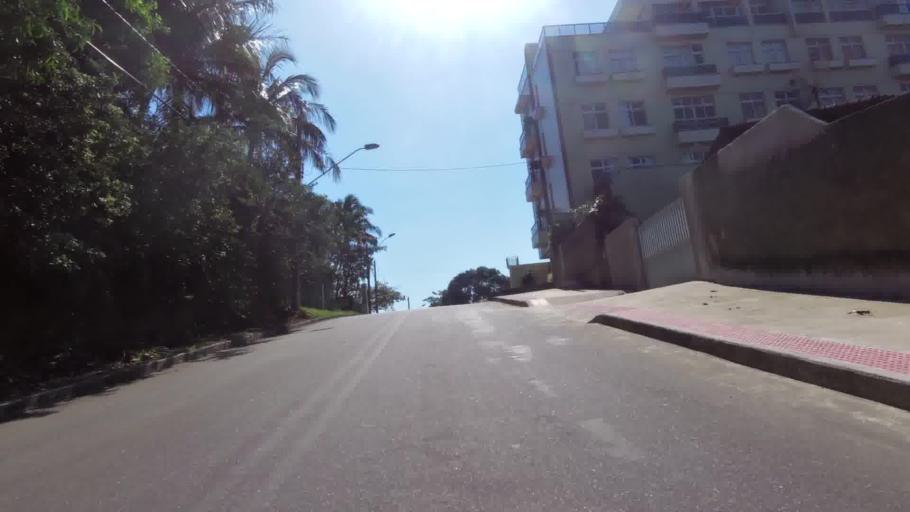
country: BR
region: Espirito Santo
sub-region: Guarapari
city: Guarapari
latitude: -20.7367
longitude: -40.5431
